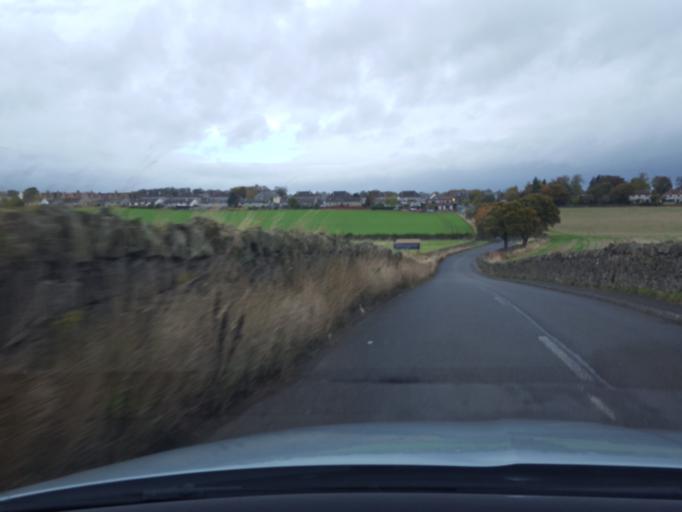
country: GB
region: Scotland
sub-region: Edinburgh
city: Ratho
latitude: 55.9174
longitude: -3.3767
